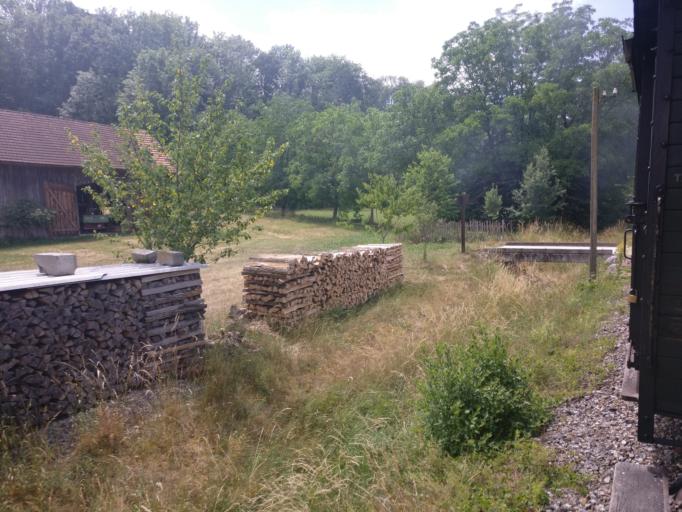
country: AT
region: Upper Austria
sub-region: Politischer Bezirk Steyr-Land
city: Sierning
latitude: 48.0223
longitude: 14.3299
